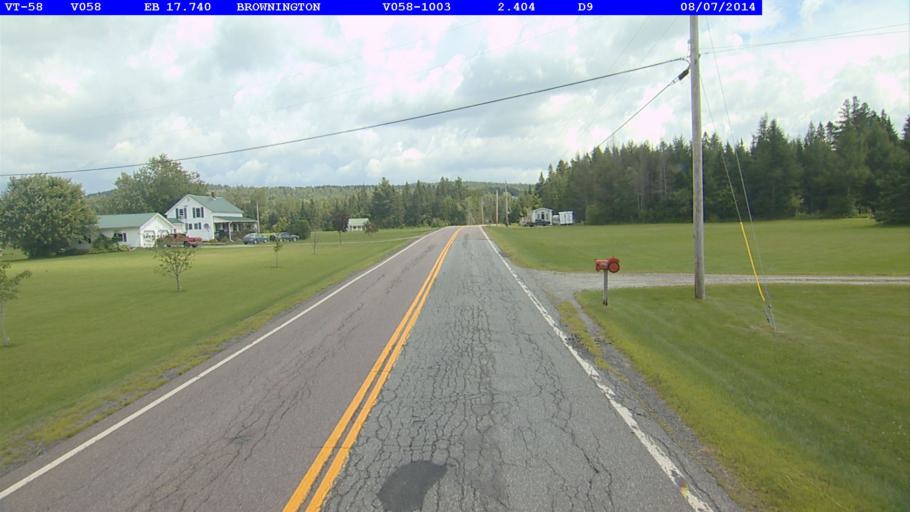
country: US
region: Vermont
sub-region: Orleans County
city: Newport
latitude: 44.7952
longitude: -72.1005
